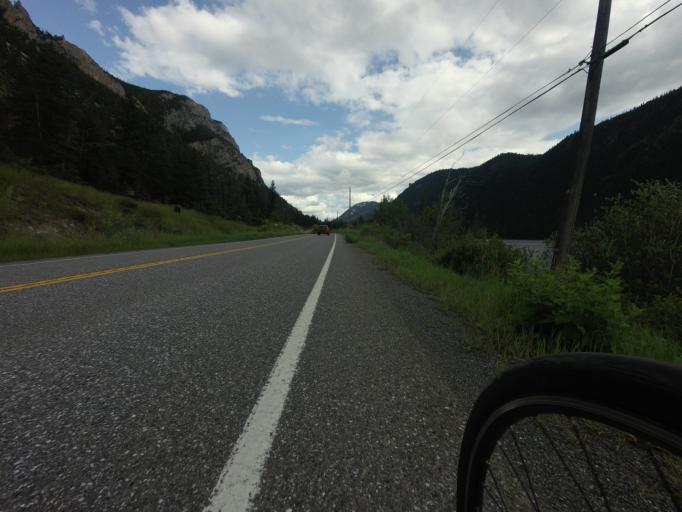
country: CA
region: British Columbia
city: Lillooet
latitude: 50.8642
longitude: -121.7318
